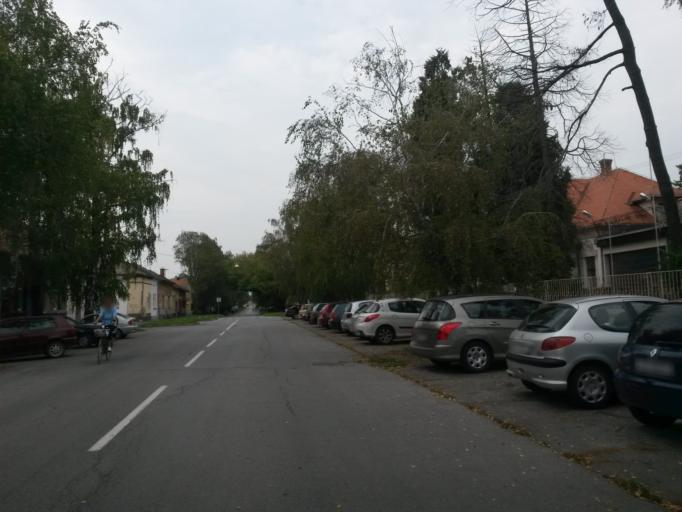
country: HR
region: Osjecko-Baranjska
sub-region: Grad Osijek
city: Osijek
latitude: 45.5510
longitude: 18.7212
